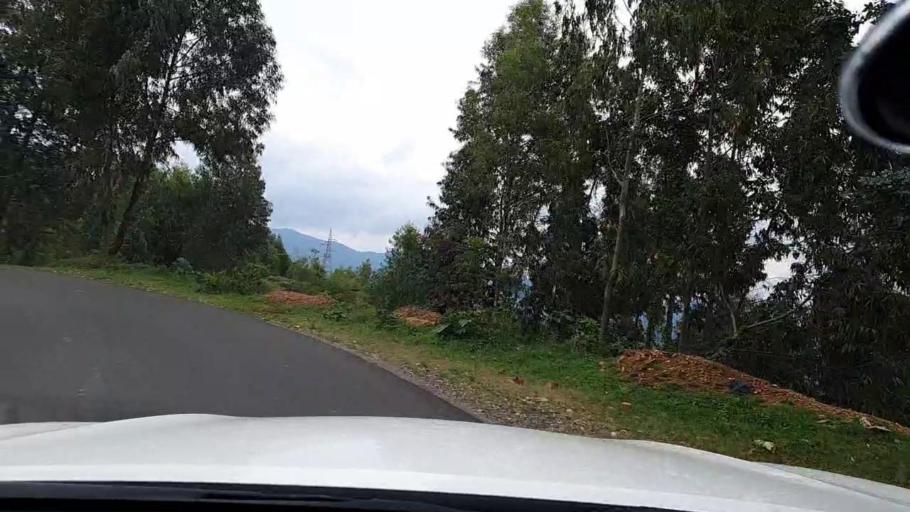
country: RW
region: Western Province
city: Kibuye
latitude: -2.1772
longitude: 29.2894
